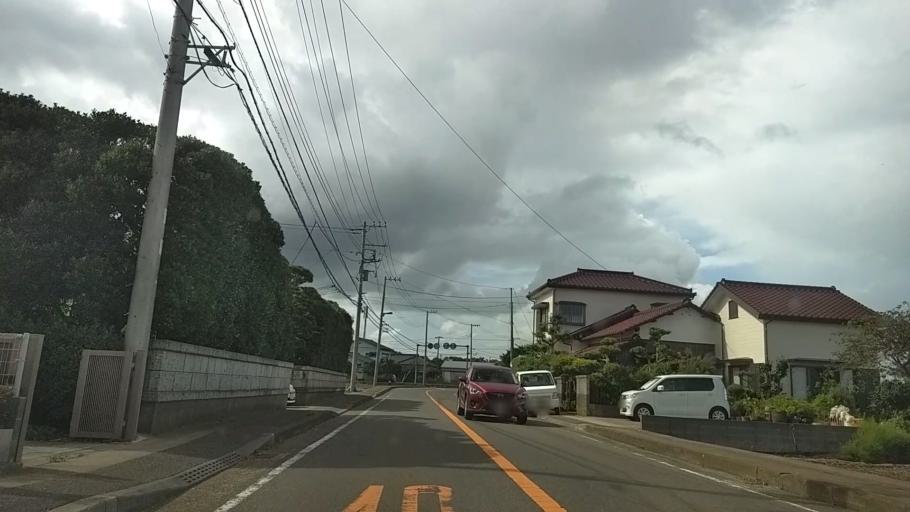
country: JP
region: Kanagawa
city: Miura
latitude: 35.1481
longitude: 139.6692
